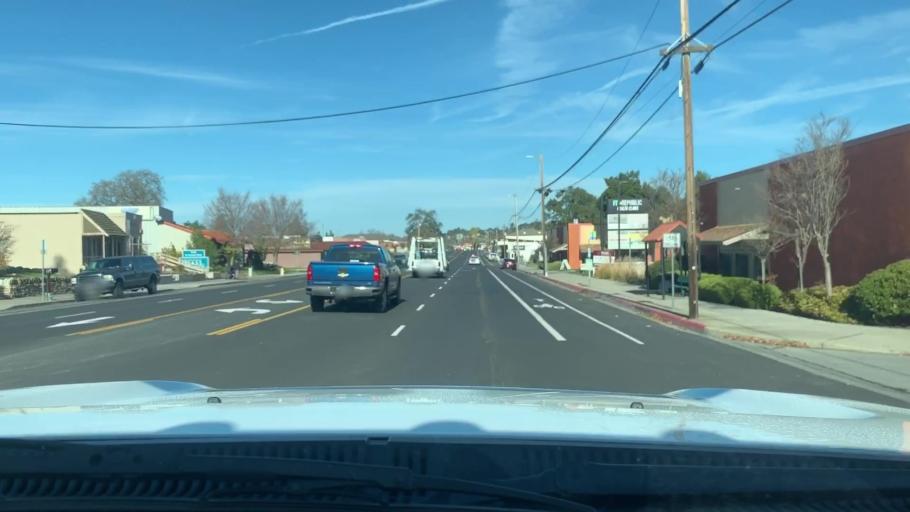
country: US
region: California
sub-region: San Luis Obispo County
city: Atascadero
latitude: 35.4717
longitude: -120.6533
